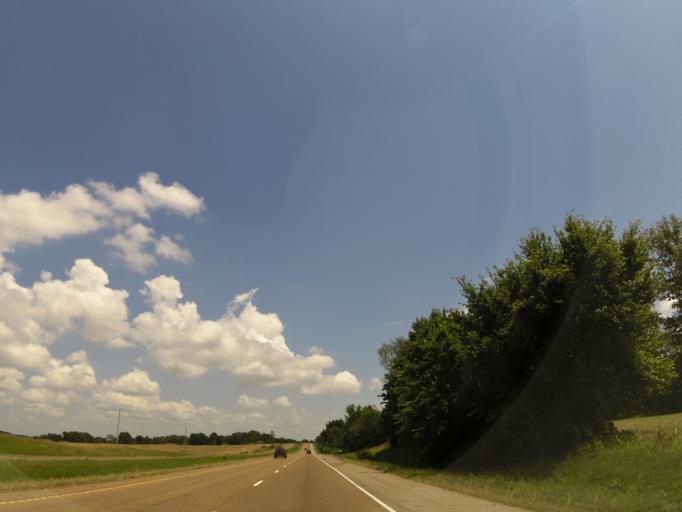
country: US
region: Tennessee
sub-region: Lauderdale County
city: Halls
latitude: 35.9438
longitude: -89.3029
